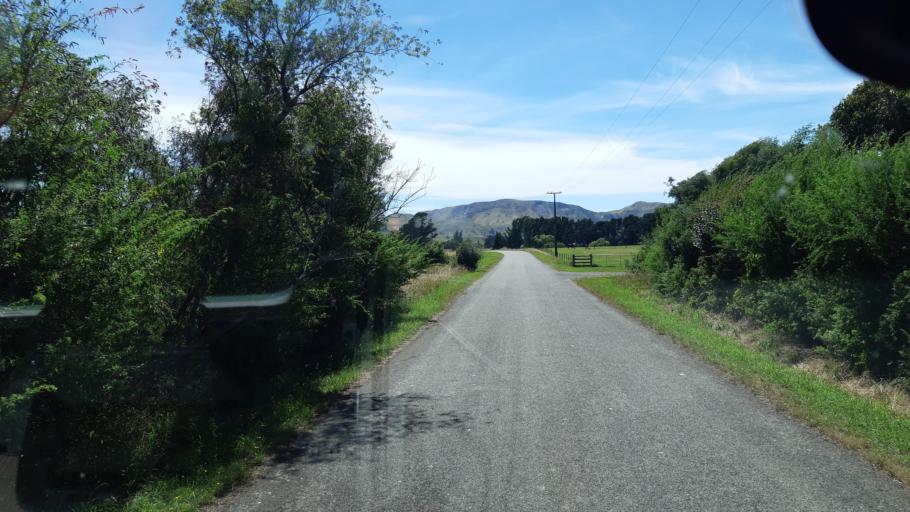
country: NZ
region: Marlborough
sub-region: Marlborough District
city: Blenheim
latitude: -41.8290
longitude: 174.1131
